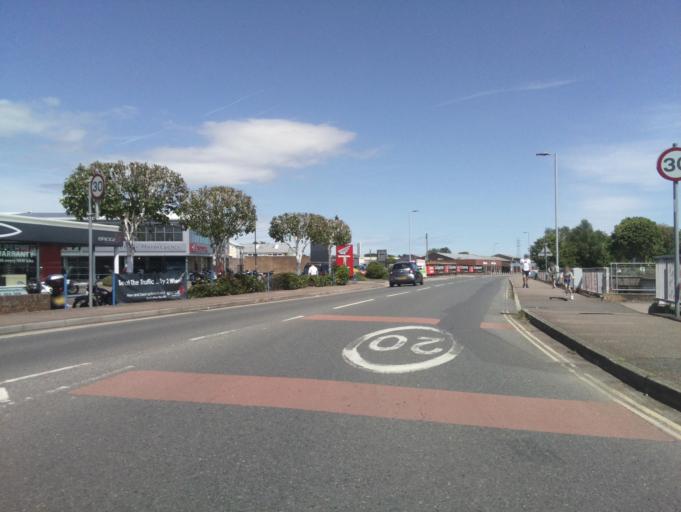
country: GB
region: England
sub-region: Devon
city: Exeter
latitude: 50.7023
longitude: -3.5333
